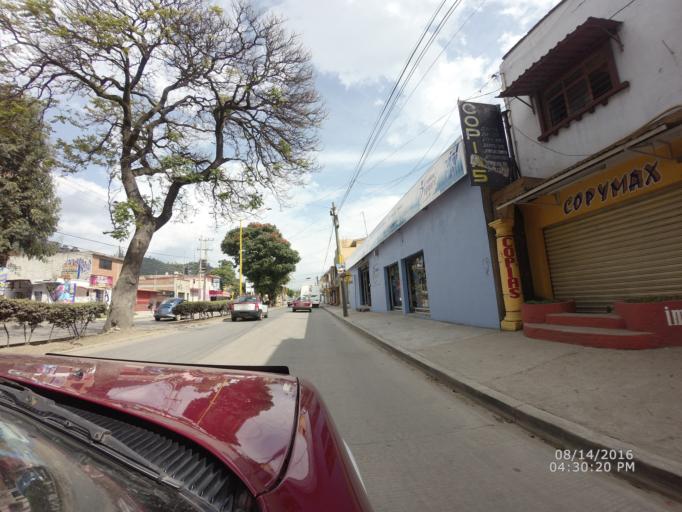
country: MX
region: Oaxaca
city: Oaxaca de Juarez
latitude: 17.0779
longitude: -96.7423
